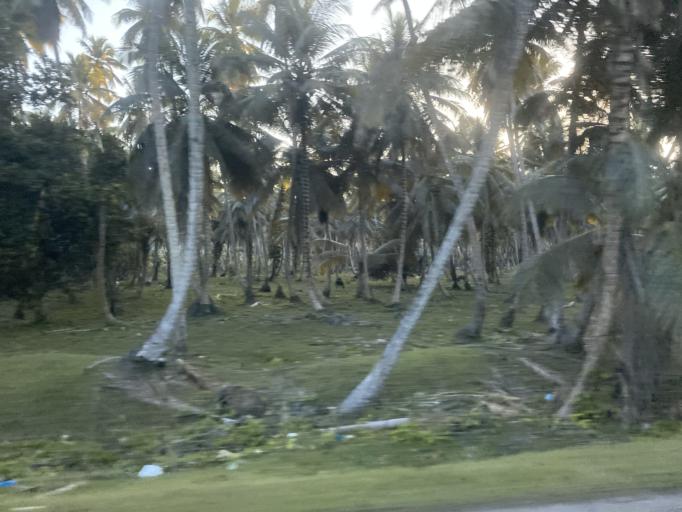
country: DO
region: Maria Trinidad Sanchez
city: Nagua
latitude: 19.3637
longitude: -69.8348
